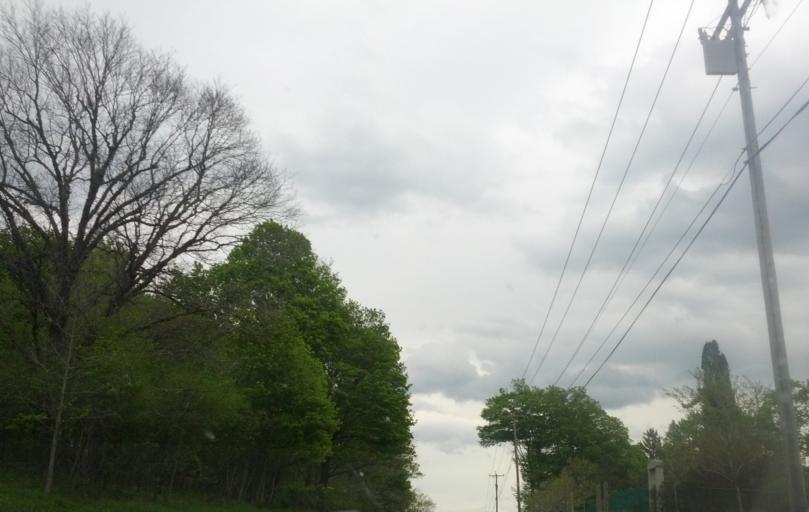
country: US
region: New York
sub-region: Onondaga County
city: Fayetteville
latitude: 42.9911
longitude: -76.0569
